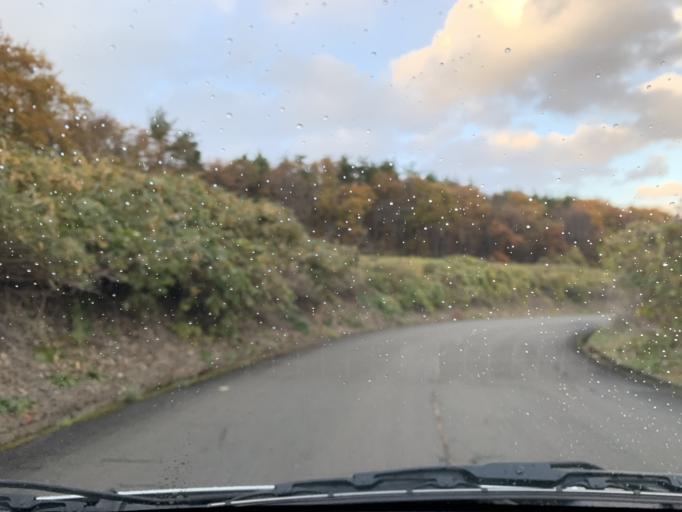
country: JP
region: Iwate
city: Mizusawa
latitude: 39.0748
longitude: 141.0299
